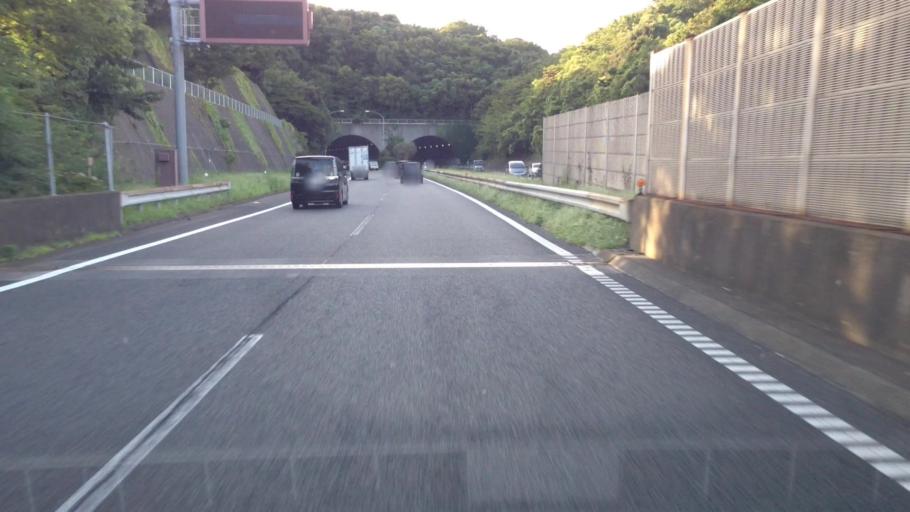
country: JP
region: Kanagawa
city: Zushi
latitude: 35.3212
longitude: 139.6038
